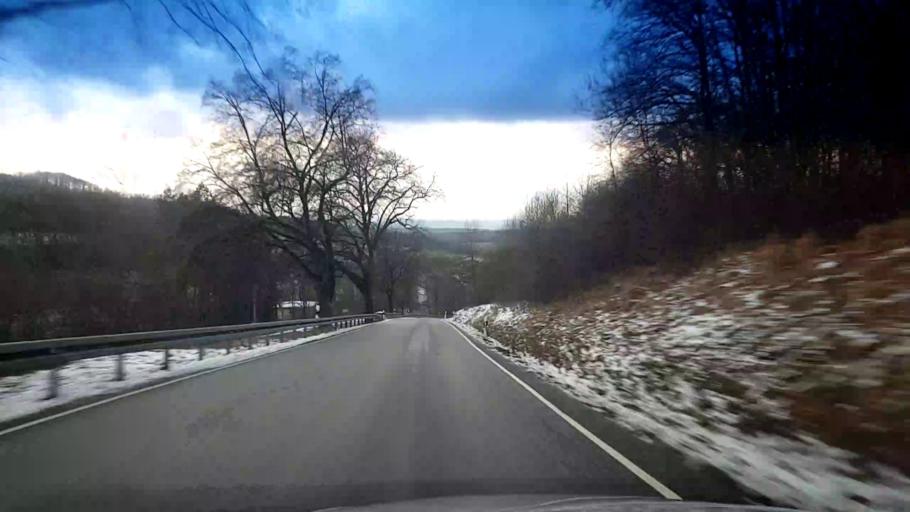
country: DE
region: Bavaria
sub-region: Upper Franconia
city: Poxdorf
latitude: 49.8698
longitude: 11.0771
